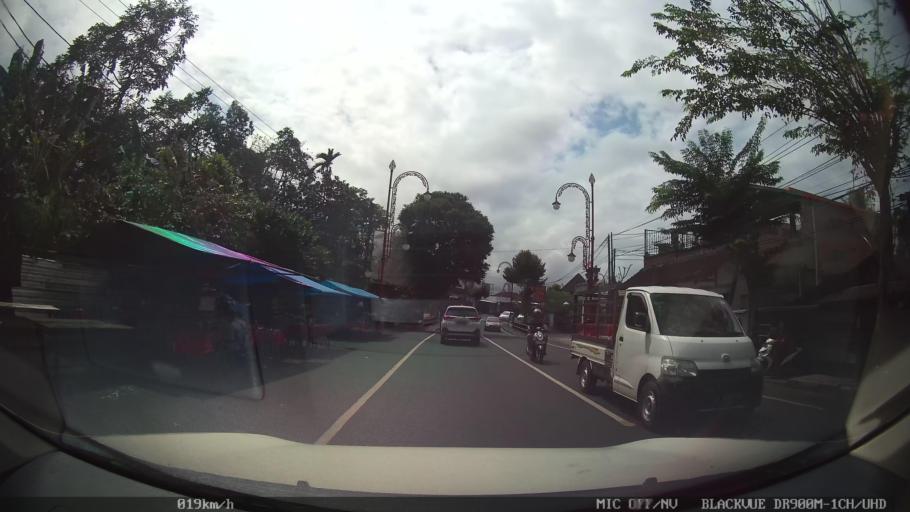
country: ID
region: Bali
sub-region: Kabupaten Gianyar
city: Ubud
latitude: -8.5327
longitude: 115.3029
